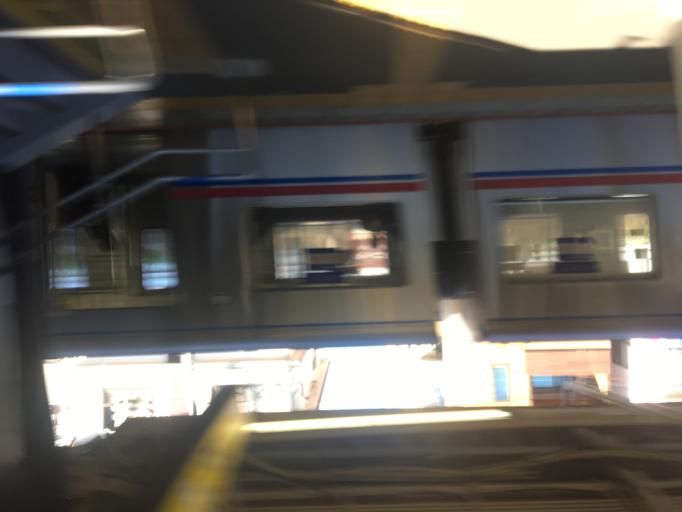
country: JP
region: Chiba
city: Funabashi
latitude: 35.7146
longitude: 139.9526
